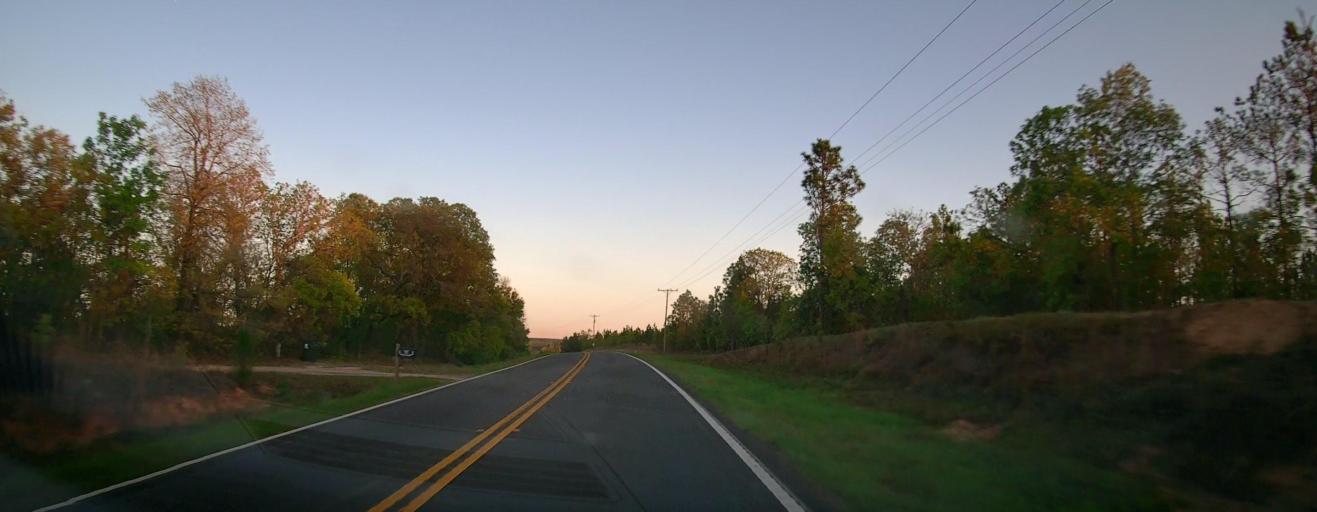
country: US
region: Georgia
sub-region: Marion County
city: Buena Vista
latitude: 32.4052
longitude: -84.5813
